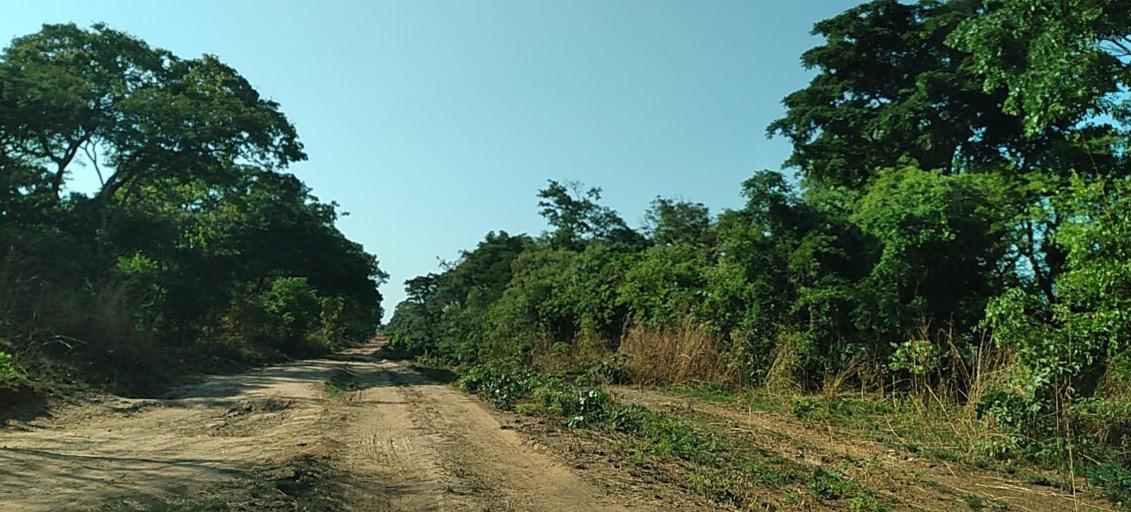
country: ZM
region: Central
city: Mkushi
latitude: -13.4595
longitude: 28.9111
